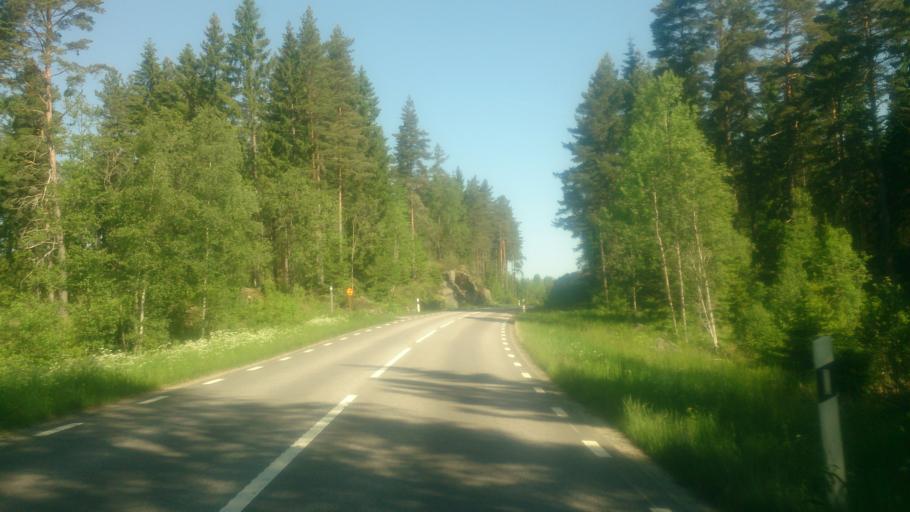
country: SE
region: OEstergoetland
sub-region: Atvidabergs Kommun
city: Atvidaberg
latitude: 58.1219
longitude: 16.0944
